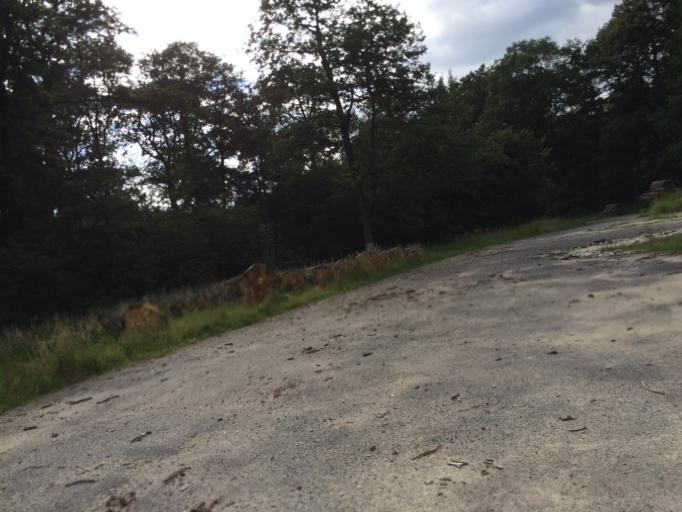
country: FR
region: Ile-de-France
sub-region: Departement de l'Essonne
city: Etiolles
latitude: 48.6575
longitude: 2.4870
